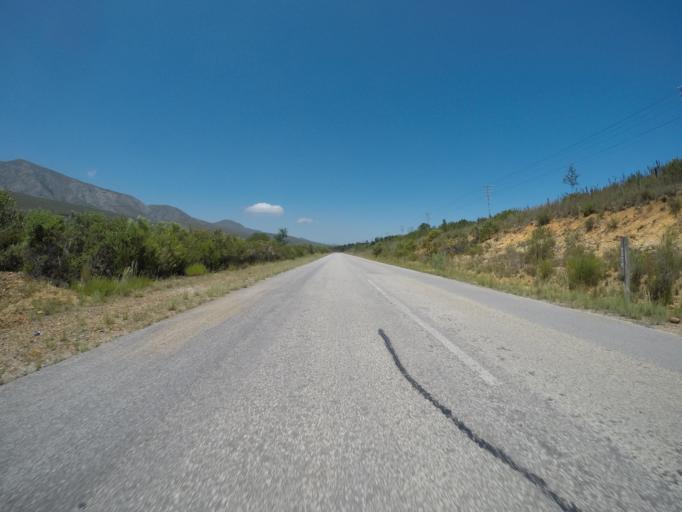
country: ZA
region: Eastern Cape
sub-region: Cacadu District Municipality
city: Kareedouw
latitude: -33.9133
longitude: 24.1763
